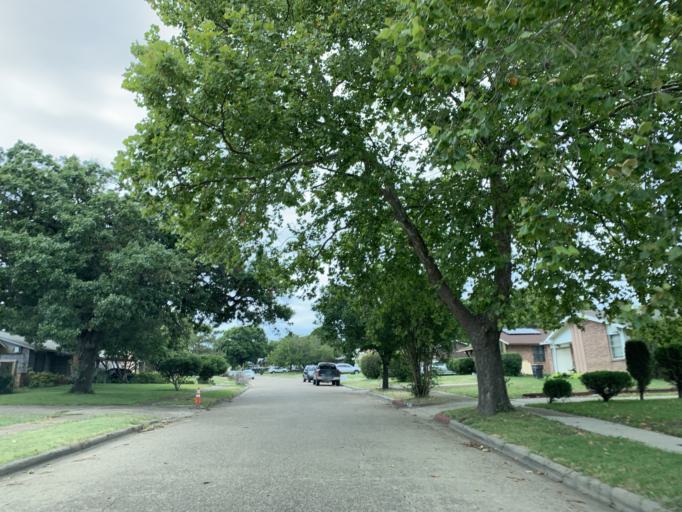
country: US
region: Texas
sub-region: Dallas County
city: DeSoto
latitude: 32.6576
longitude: -96.8282
